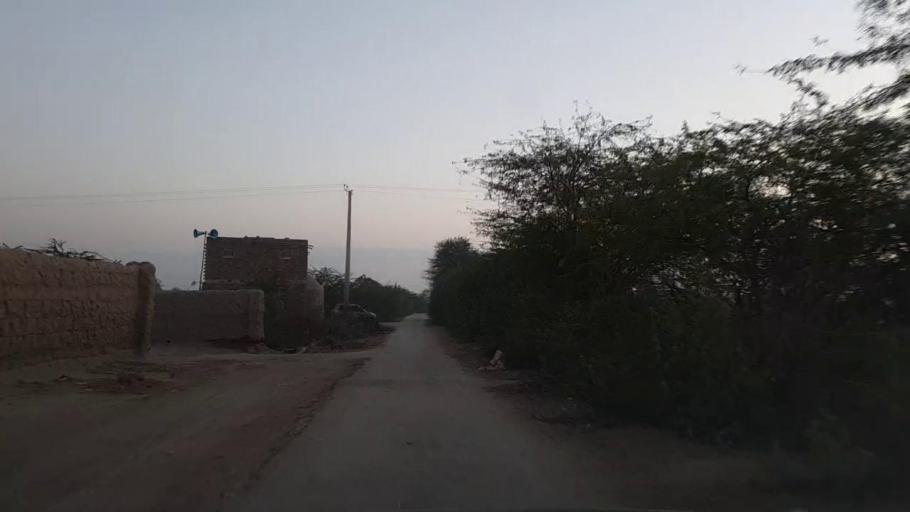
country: PK
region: Sindh
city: Daur
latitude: 26.4852
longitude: 68.4906
